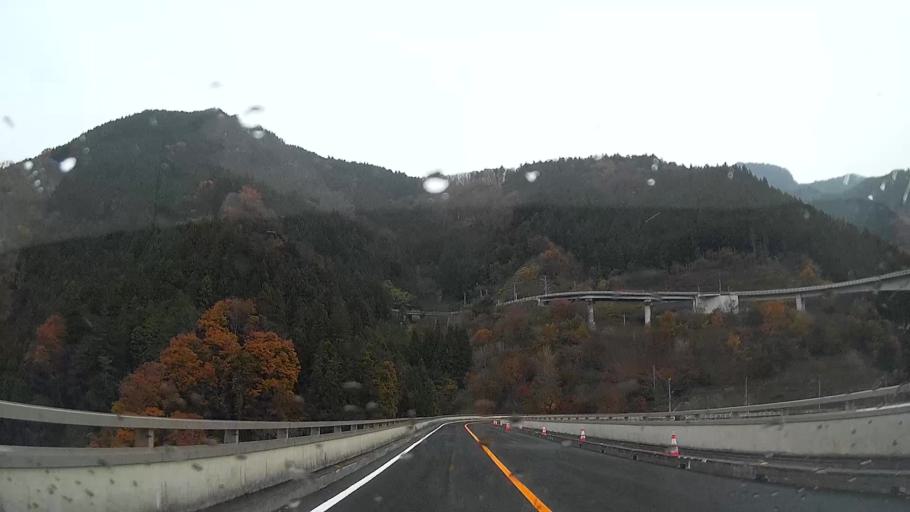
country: JP
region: Saitama
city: Chichibu
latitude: 35.9562
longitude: 138.9026
